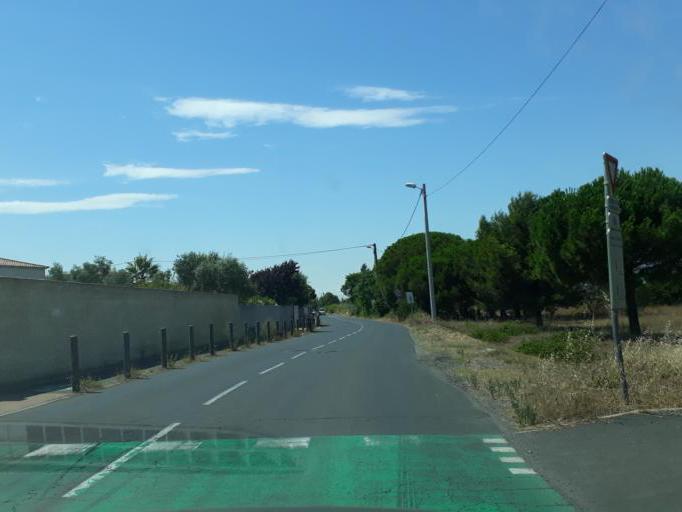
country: FR
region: Languedoc-Roussillon
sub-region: Departement de l'Herault
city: Agde
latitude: 43.2890
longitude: 3.4706
